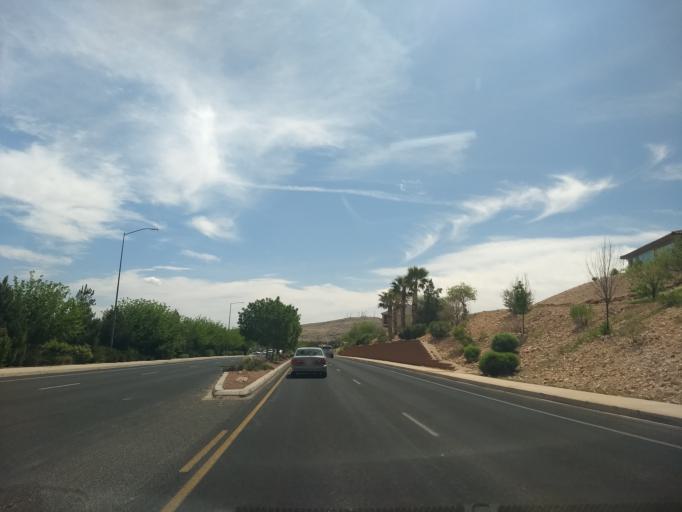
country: US
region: Utah
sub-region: Washington County
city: Saint George
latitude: 37.0773
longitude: -113.6008
